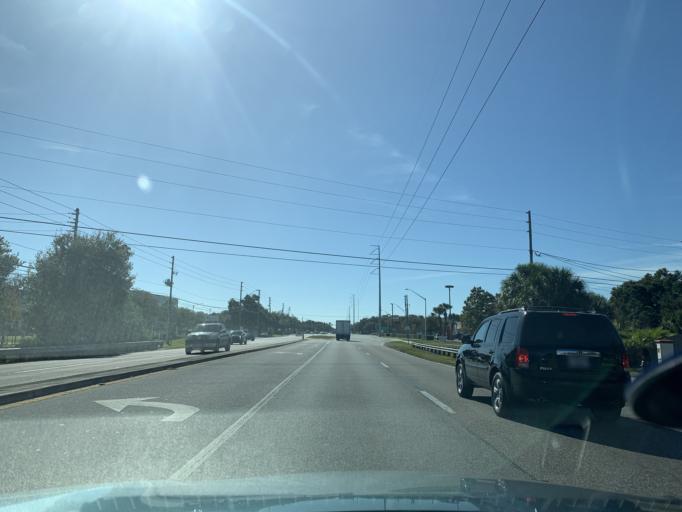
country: US
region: Florida
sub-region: Pinellas County
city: Largo
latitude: 27.8755
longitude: -82.7624
